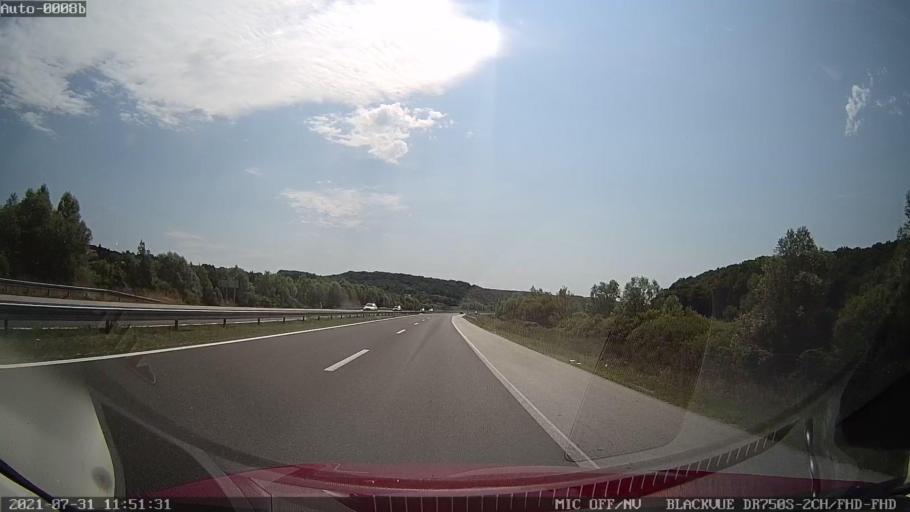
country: HR
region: Varazdinska
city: Remetinec
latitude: 46.0784
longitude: 16.2924
